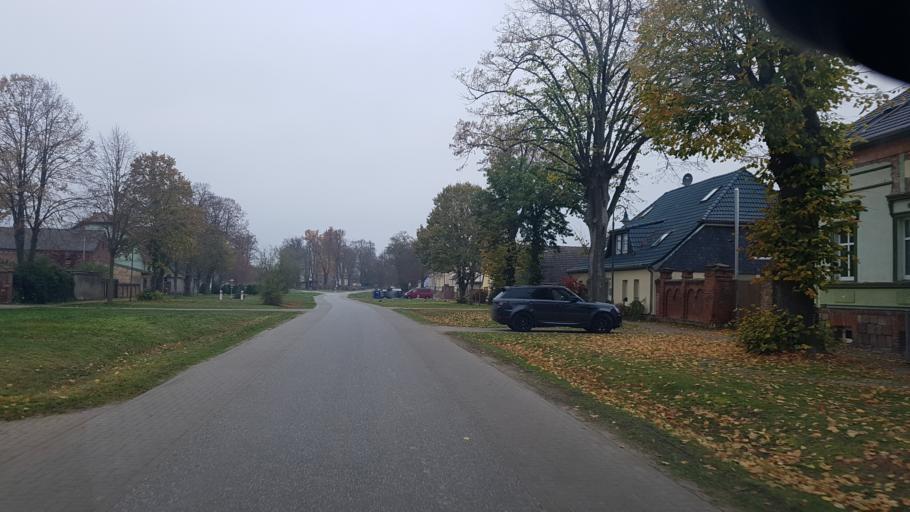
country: DE
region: Brandenburg
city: Schonermark
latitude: 52.9308
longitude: 13.1136
